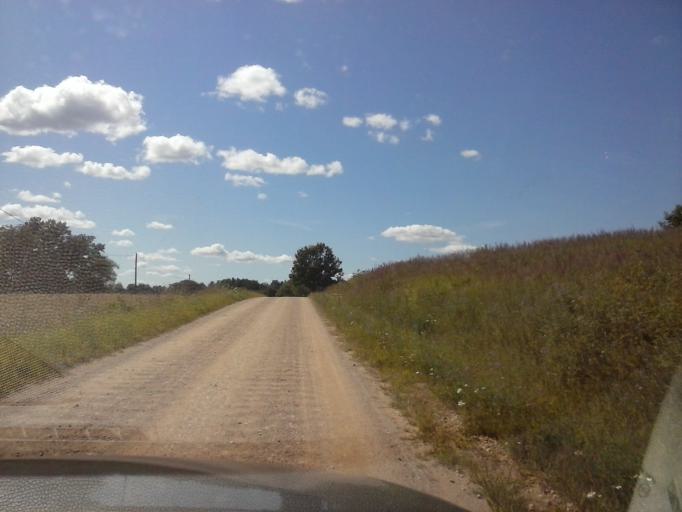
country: LV
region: Apes Novads
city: Ape
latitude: 57.5717
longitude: 26.6815
